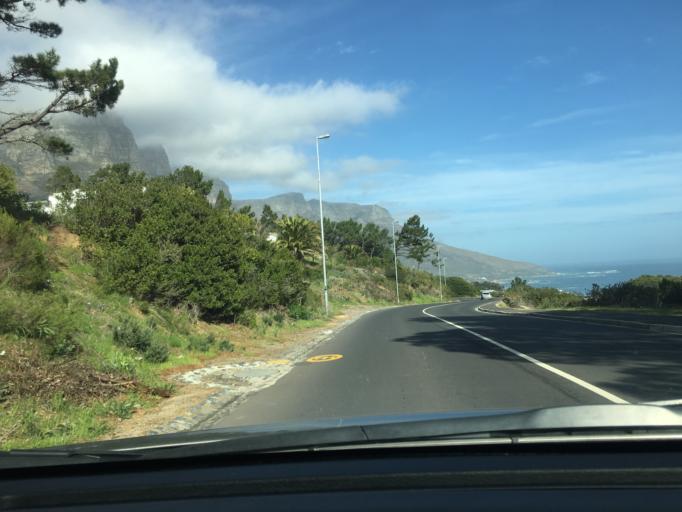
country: ZA
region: Western Cape
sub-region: City of Cape Town
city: Cape Town
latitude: -33.9591
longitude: 18.3820
